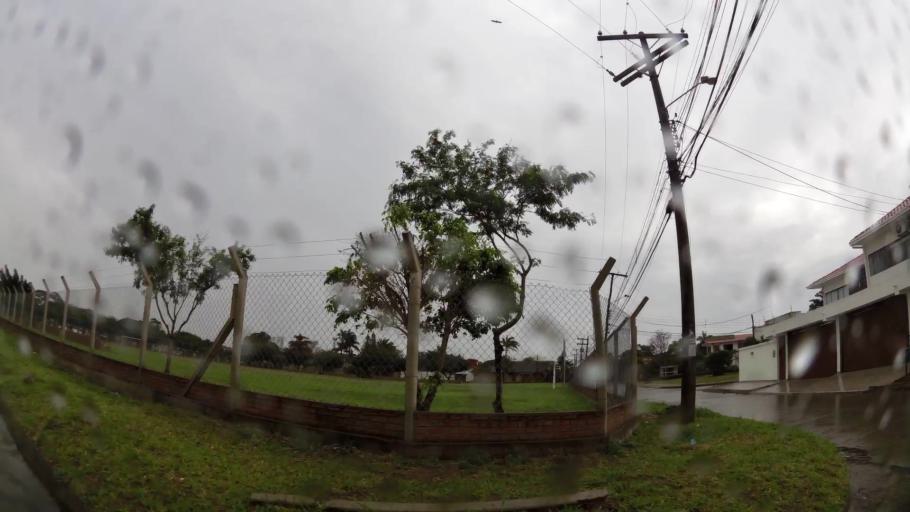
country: BO
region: Santa Cruz
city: Santa Cruz de la Sierra
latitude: -17.8063
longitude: -63.1580
